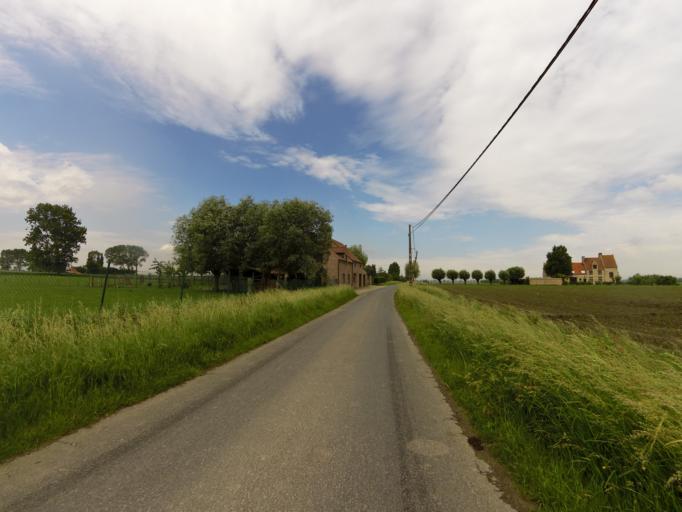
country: BE
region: Flanders
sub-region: Provincie West-Vlaanderen
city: Middelkerke
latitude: 51.1459
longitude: 2.8354
